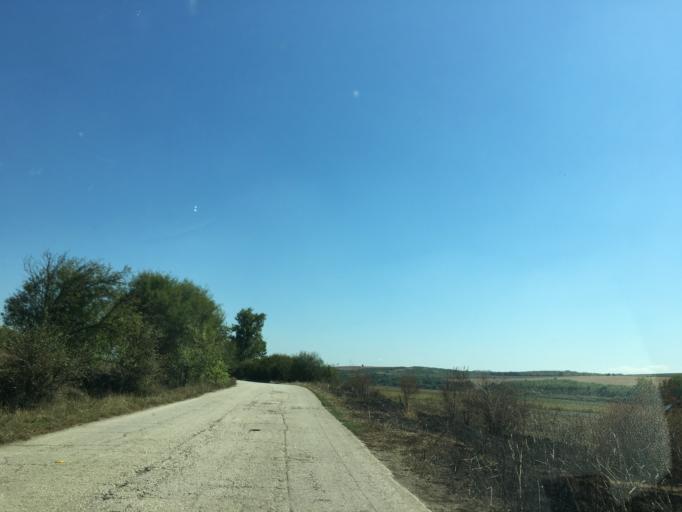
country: BG
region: Pleven
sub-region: Obshtina Knezha
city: Knezha
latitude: 43.5381
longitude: 24.1143
